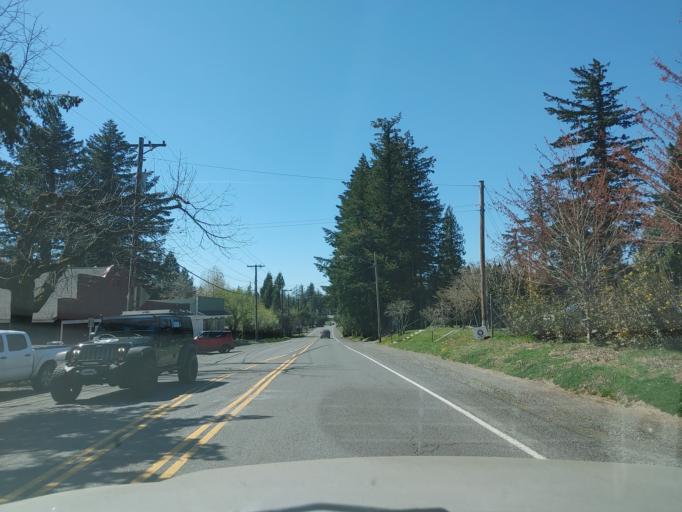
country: US
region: Oregon
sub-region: Multnomah County
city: Troutdale
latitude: 45.5190
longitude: -122.3301
